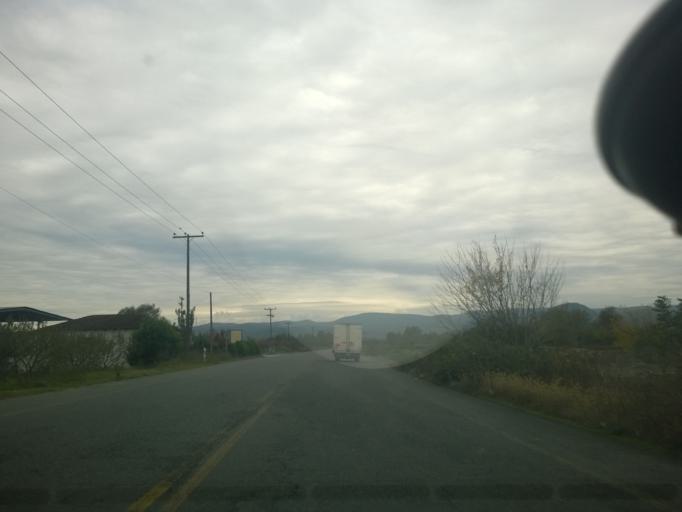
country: GR
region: Central Macedonia
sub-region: Nomos Pellis
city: Apsalos
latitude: 40.9248
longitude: 22.0824
